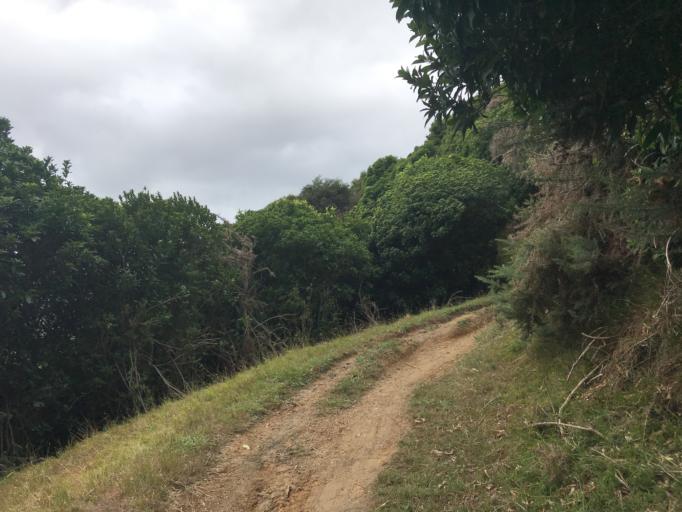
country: NZ
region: Marlborough
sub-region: Marlborough District
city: Picton
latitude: -41.2351
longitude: 173.9593
